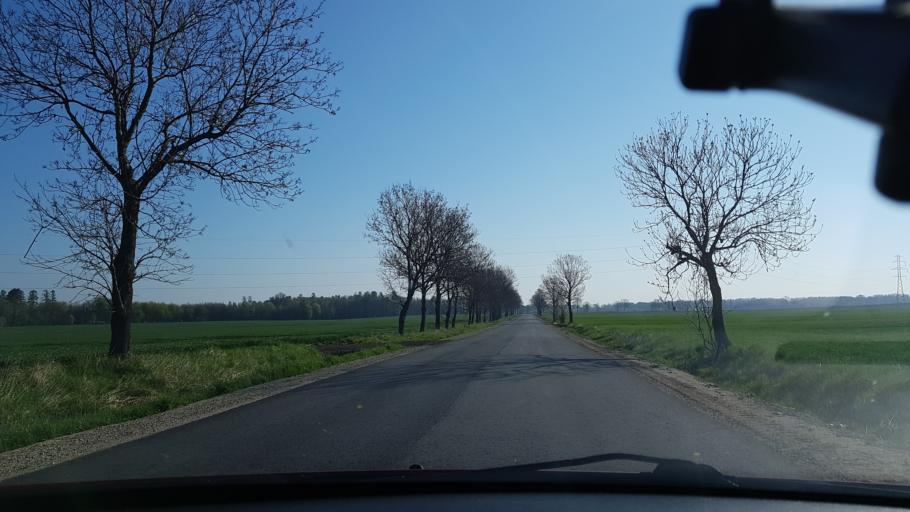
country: CZ
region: Olomoucky
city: Vidnava
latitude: 50.4238
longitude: 17.2333
